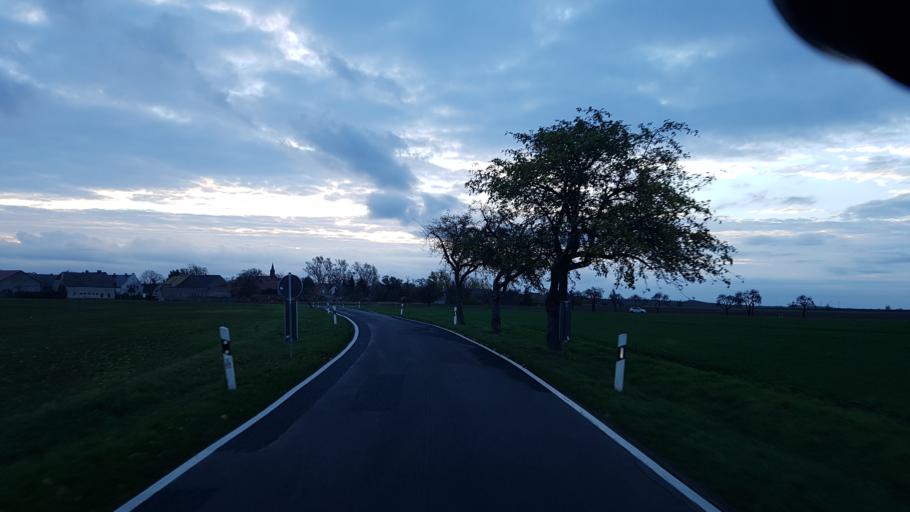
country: DE
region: Brandenburg
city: Muhlberg
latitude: 51.4615
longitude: 13.2524
